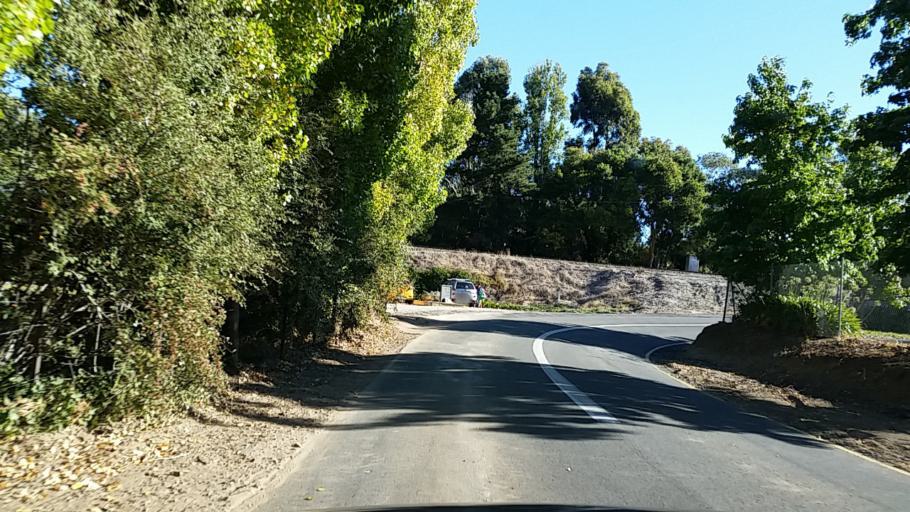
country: AU
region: South Australia
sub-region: Mount Barker
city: Nairne
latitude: -35.0385
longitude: 138.9180
